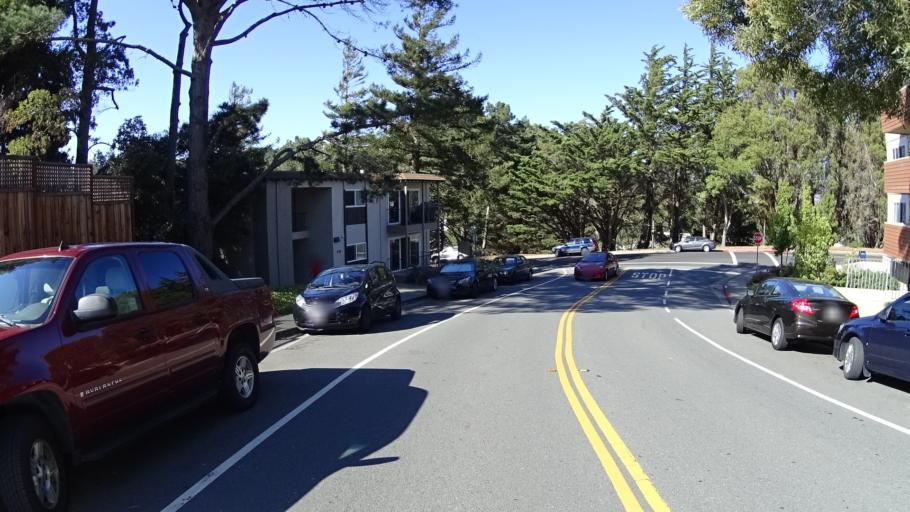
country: US
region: California
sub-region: San Mateo County
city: San Bruno
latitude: 37.6178
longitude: -122.4276
